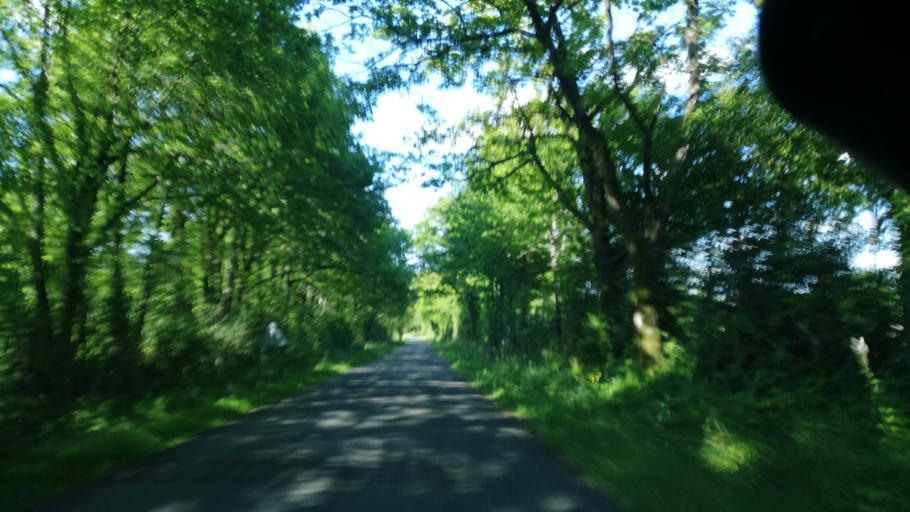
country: FR
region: Poitou-Charentes
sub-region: Departement des Deux-Sevres
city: Moncoutant
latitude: 46.6659
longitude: -0.5718
